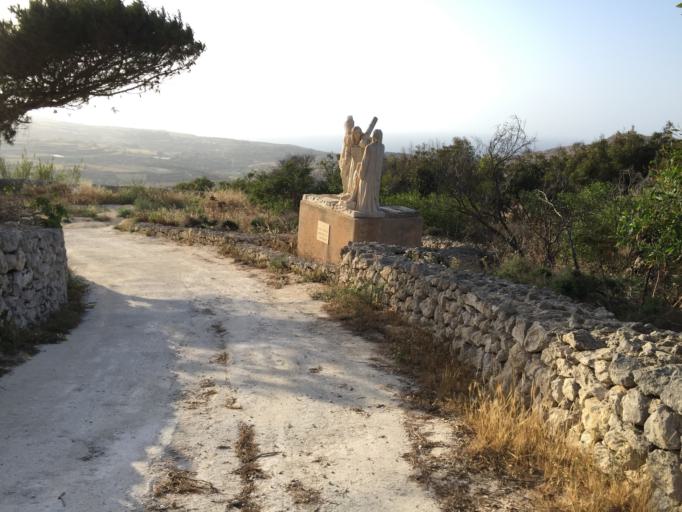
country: MT
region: L-Gharb
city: Gharb
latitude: 36.0604
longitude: 14.2193
